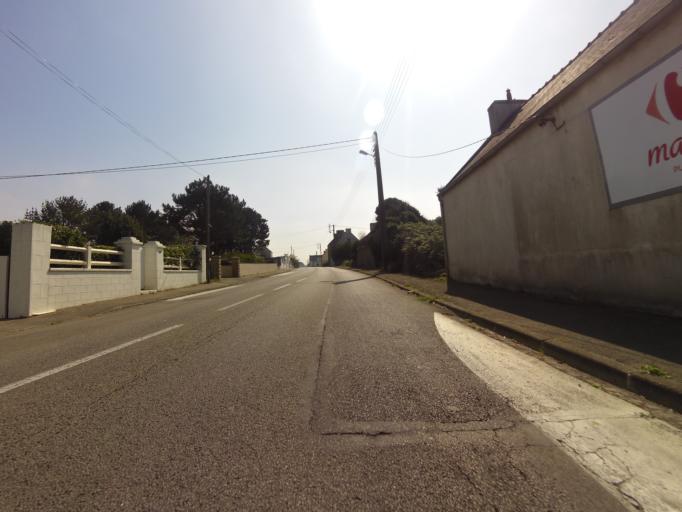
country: FR
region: Brittany
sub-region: Departement du Finistere
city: Plouhinec
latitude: 48.0158
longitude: -4.4986
